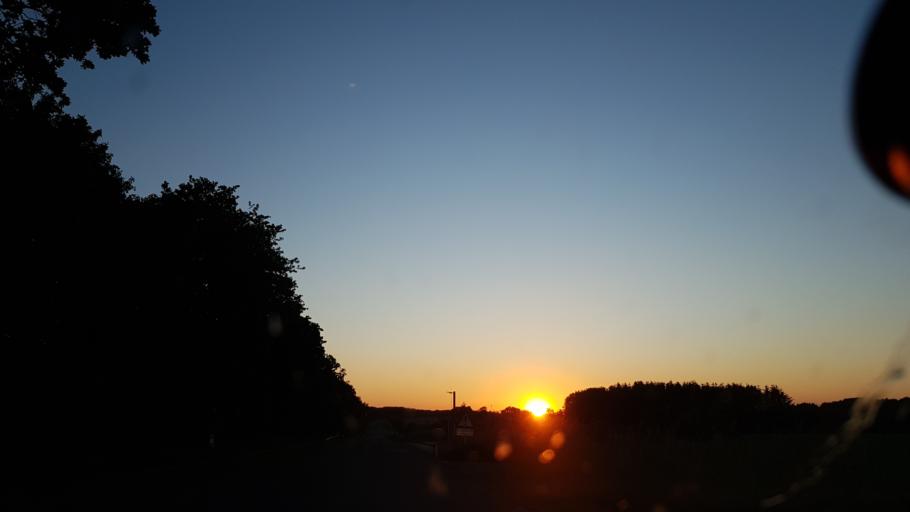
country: DK
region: South Denmark
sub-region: Tonder Kommune
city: Toftlund
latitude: 55.1331
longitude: 9.1355
